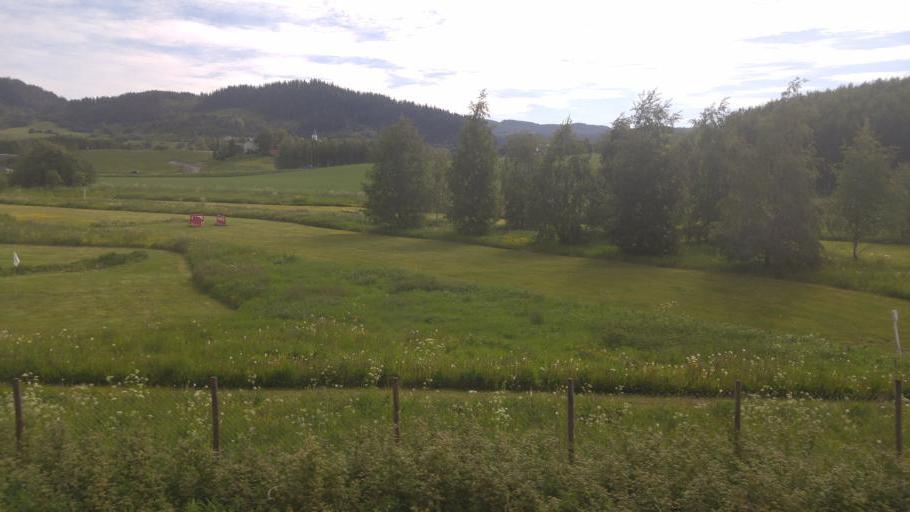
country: NO
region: Sor-Trondelag
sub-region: Melhus
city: Lundamo
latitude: 63.1950
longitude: 10.2974
